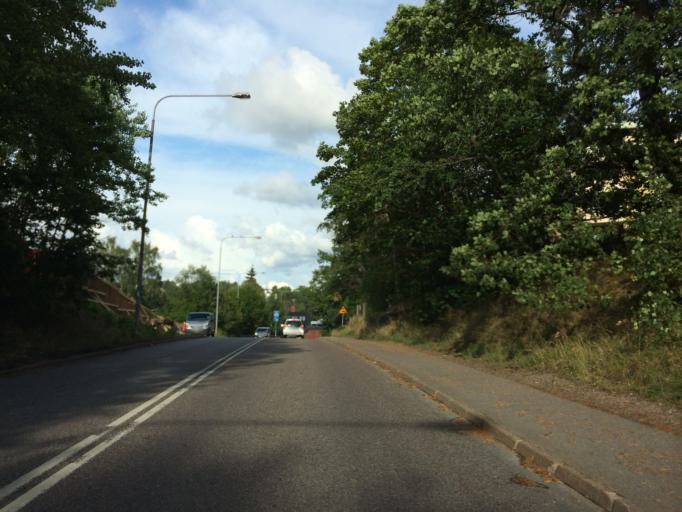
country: SE
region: Stockholm
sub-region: Huddinge Kommun
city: Segeltorp
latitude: 59.2802
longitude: 17.9446
